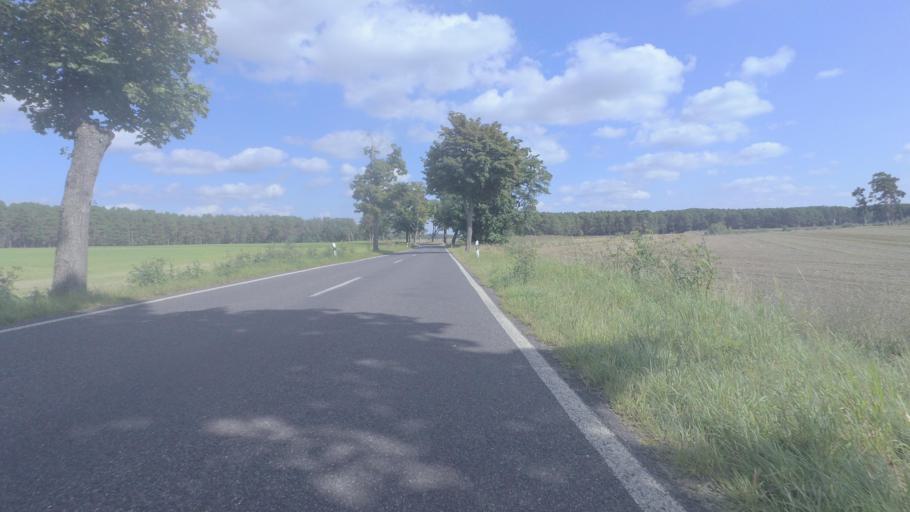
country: DE
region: Brandenburg
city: Munchehofe
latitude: 52.1505
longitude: 13.8478
